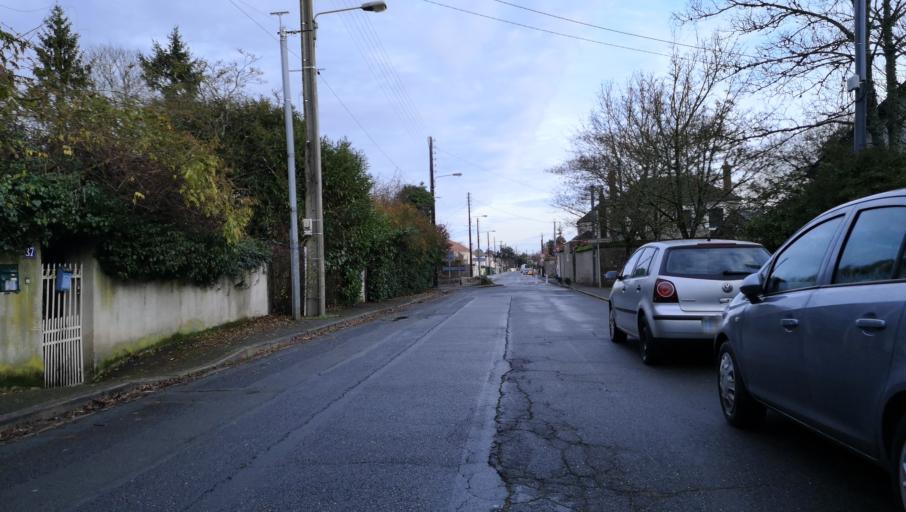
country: FR
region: Centre
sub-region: Departement du Loiret
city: Semoy
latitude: 47.9129
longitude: 1.9553
